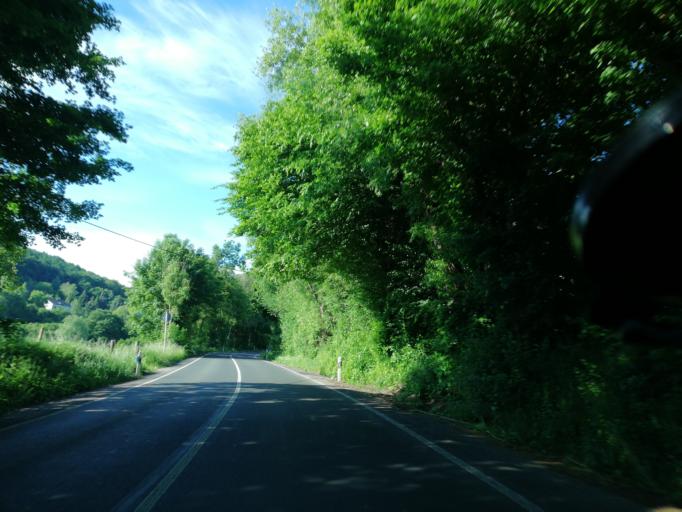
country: DE
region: North Rhine-Westphalia
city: Wetter (Ruhr)
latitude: 51.3857
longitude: 7.3361
